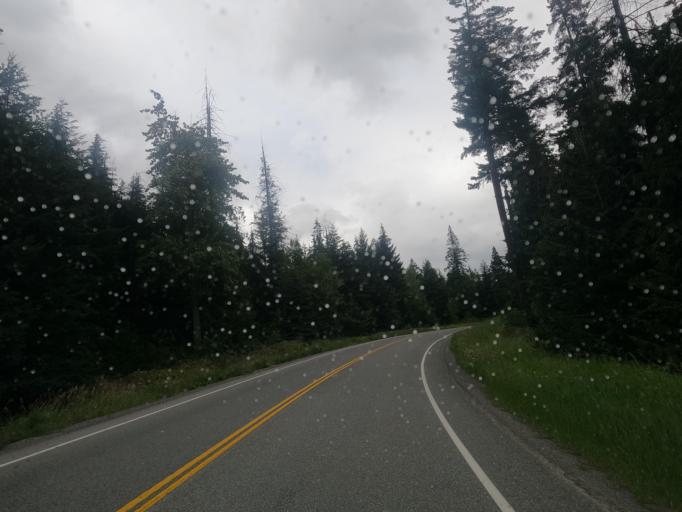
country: CA
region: British Columbia
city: Lillooet
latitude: 50.5043
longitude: -122.1809
